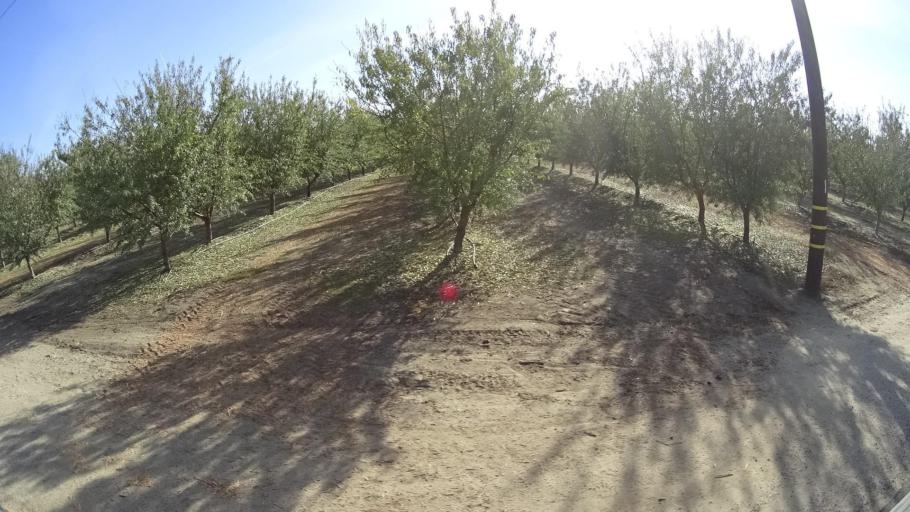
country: US
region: California
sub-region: Kern County
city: McFarland
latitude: 35.7032
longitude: -119.3229
